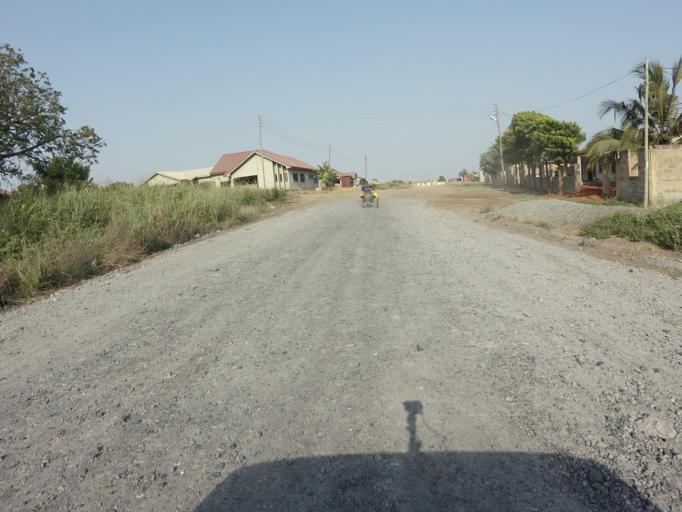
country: GH
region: Greater Accra
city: Tema
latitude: 5.7015
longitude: 0.0608
